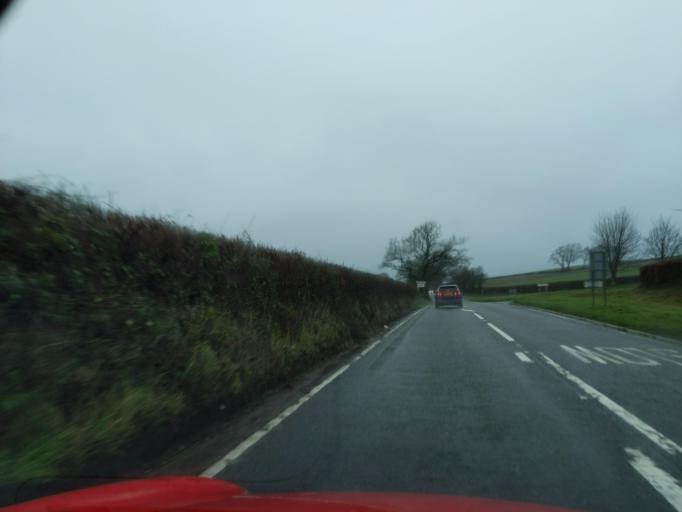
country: GB
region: England
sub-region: Cornwall
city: Launceston
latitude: 50.6149
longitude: -4.3399
